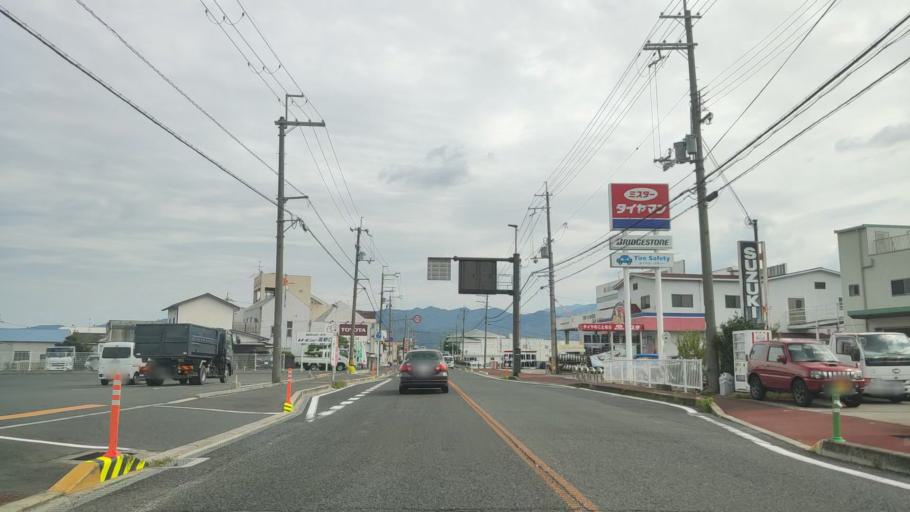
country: JP
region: Wakayama
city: Hashimoto
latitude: 34.3053
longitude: 135.5472
